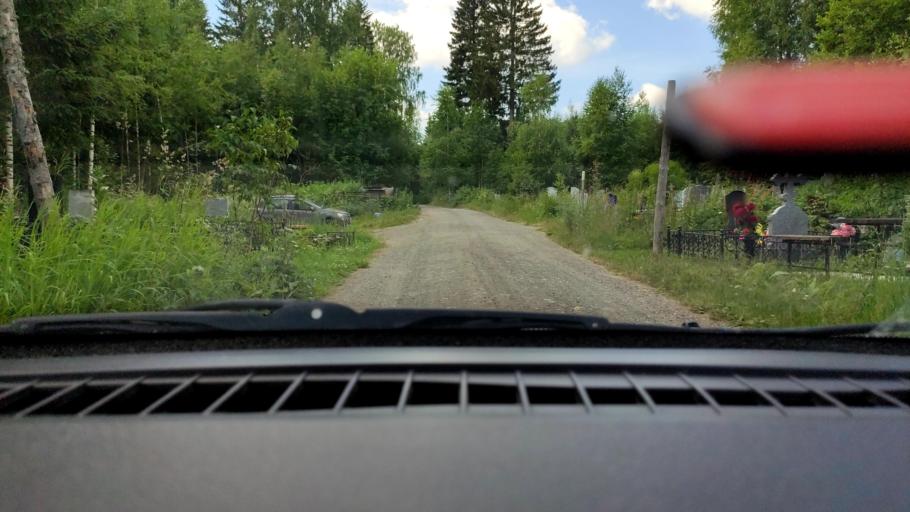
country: RU
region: Perm
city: Perm
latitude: 58.1453
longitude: 56.2839
